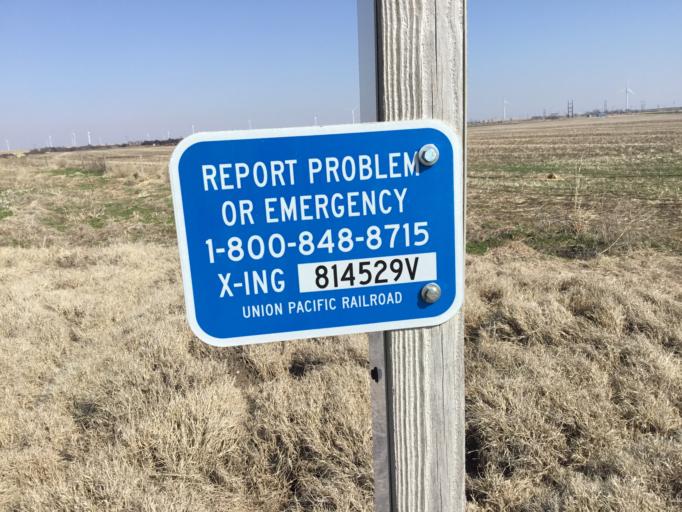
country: US
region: Kansas
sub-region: Ellsworth County
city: Ellsworth
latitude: 38.7836
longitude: -98.3980
